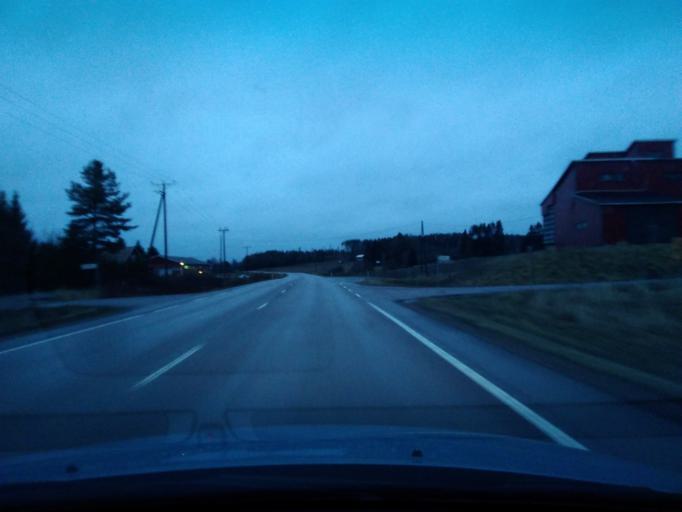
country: FI
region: Uusimaa
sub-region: Porvoo
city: Askola
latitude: 60.4606
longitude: 25.5791
